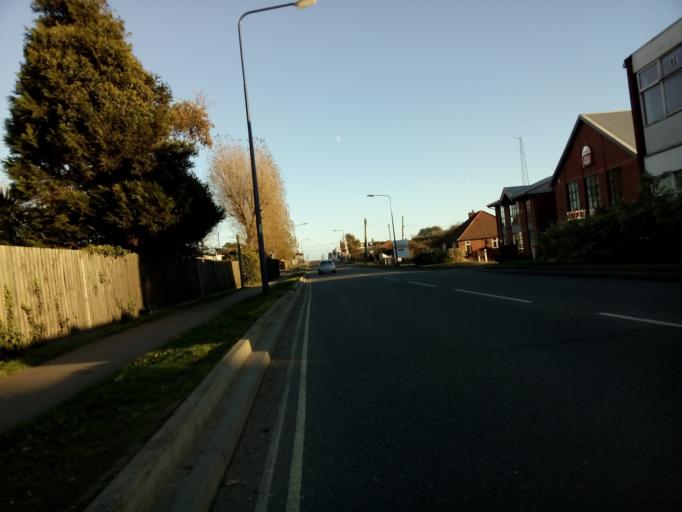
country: GB
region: England
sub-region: Suffolk
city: Felixstowe
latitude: 51.9538
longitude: 1.3319
